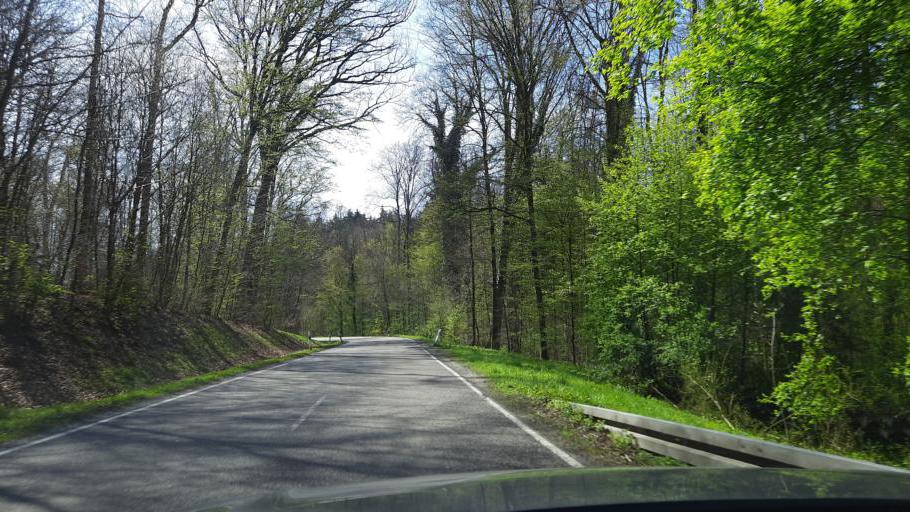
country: DE
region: Baden-Wuerttemberg
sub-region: Regierungsbezirk Stuttgart
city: Mockmuhl
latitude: 49.2798
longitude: 9.3647
